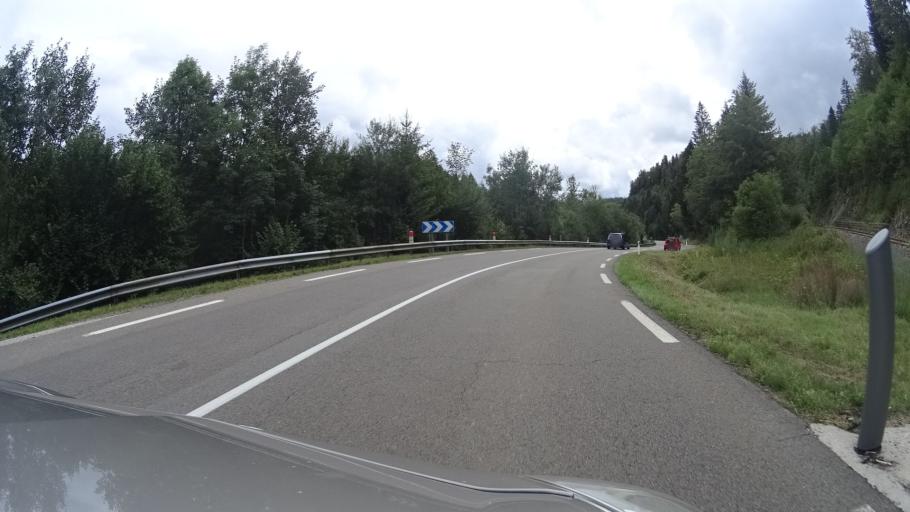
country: FR
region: Franche-Comte
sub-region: Departement du Jura
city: Champagnole
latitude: 46.6490
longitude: 5.9421
